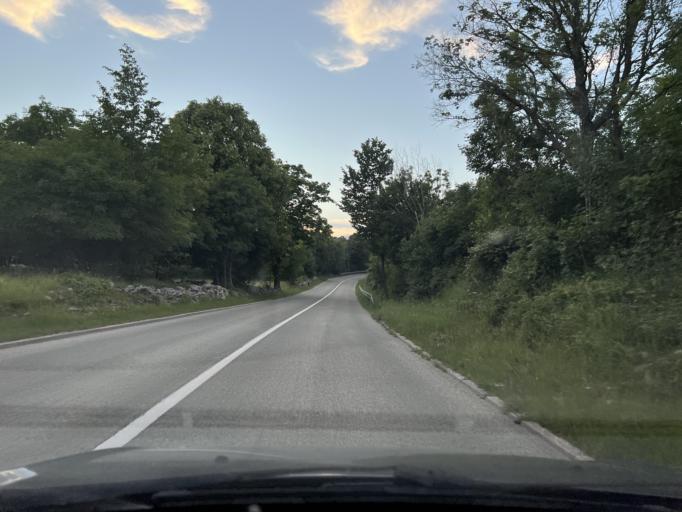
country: HR
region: Primorsko-Goranska
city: Klana
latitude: 45.4539
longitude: 14.3161
